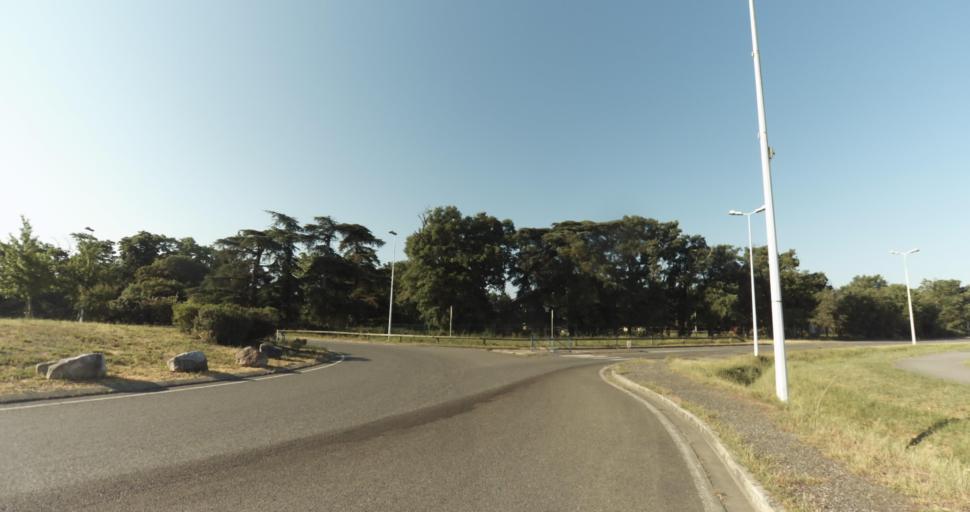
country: FR
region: Midi-Pyrenees
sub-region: Departement de la Haute-Garonne
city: La Salvetat-Saint-Gilles
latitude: 43.5702
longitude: 1.2452
